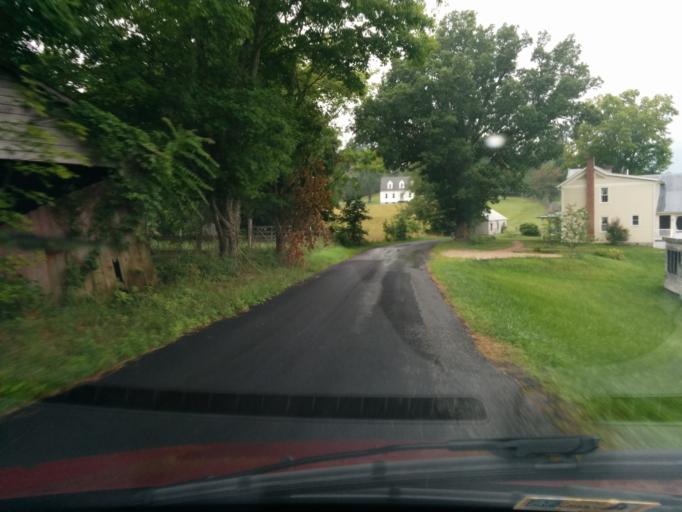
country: US
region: Virginia
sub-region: Rockbridge County
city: East Lexington
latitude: 37.8703
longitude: -79.4288
